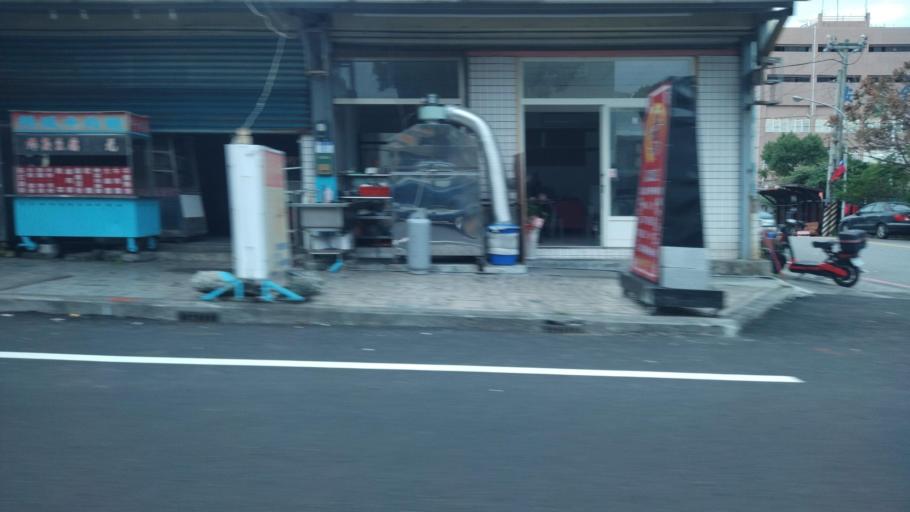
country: TW
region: Taiwan
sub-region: Hualien
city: Hualian
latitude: 24.0051
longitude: 121.6187
